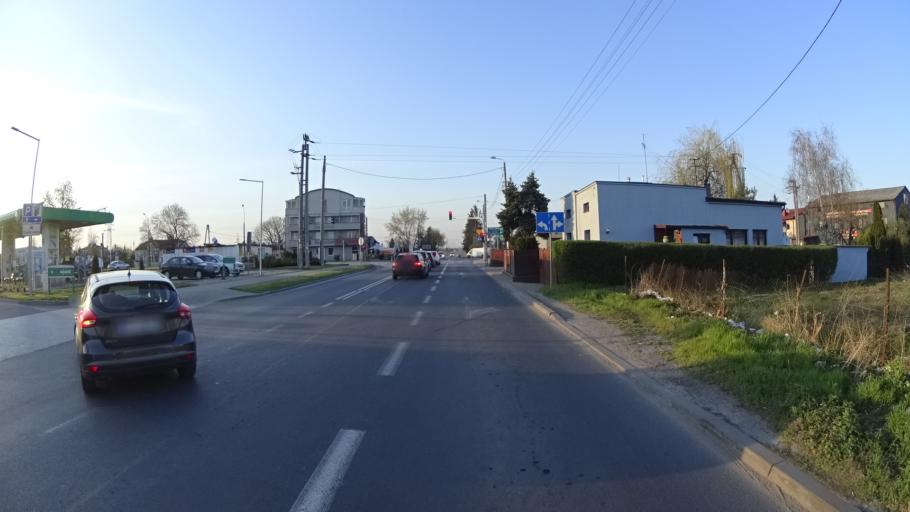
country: PL
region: Masovian Voivodeship
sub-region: Powiat warszawski zachodni
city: Ozarow Mazowiecki
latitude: 52.2093
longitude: 20.8105
